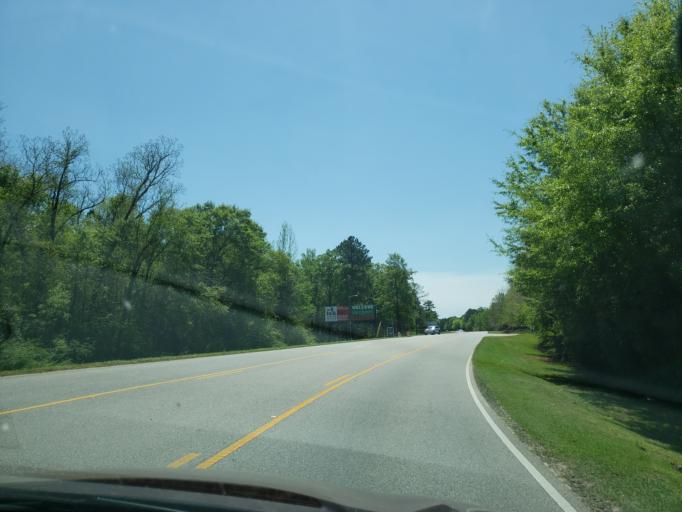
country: US
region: Alabama
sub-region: Lee County
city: Auburn
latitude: 32.6563
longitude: -85.5165
